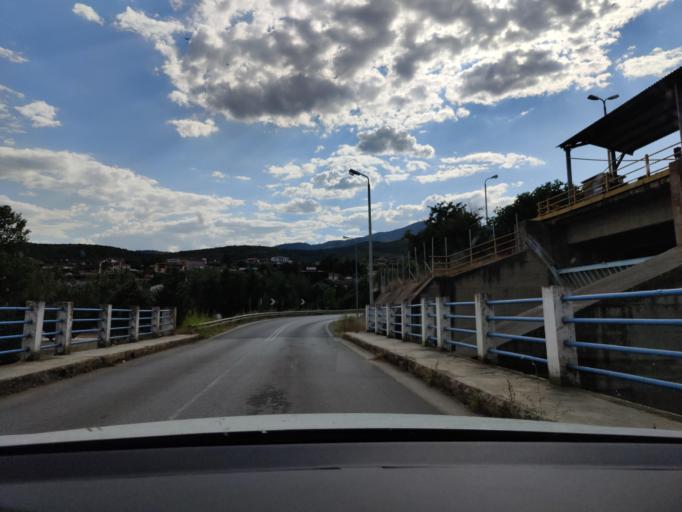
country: GR
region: Central Macedonia
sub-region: Nomos Serron
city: Chrysochorafa
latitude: 41.1379
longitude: 23.2237
